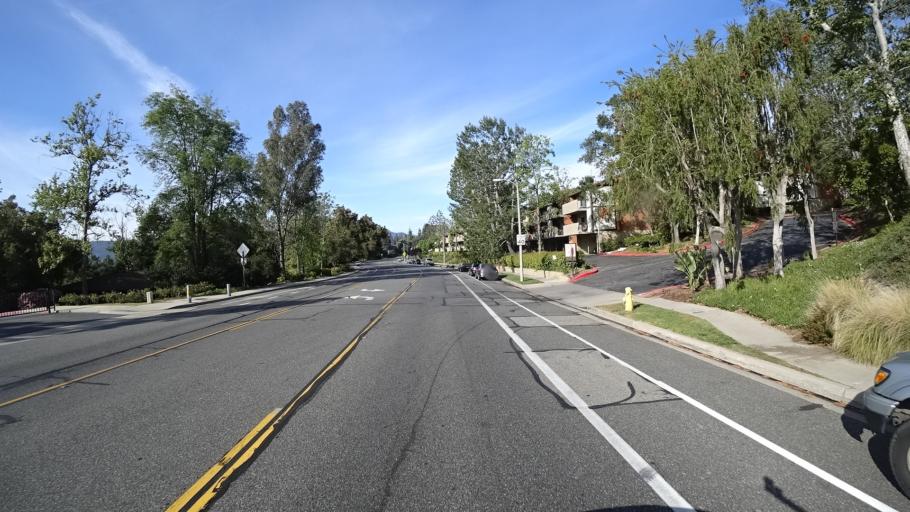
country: US
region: California
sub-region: Ventura County
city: Thousand Oaks
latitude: 34.1931
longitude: -118.8879
